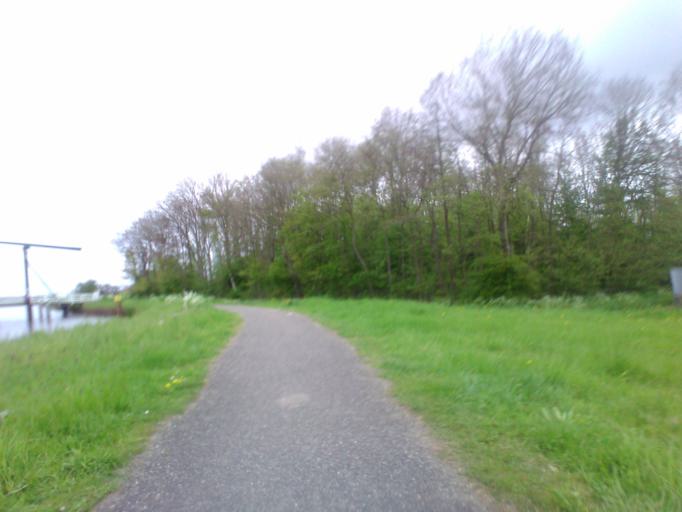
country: NL
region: South Holland
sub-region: Gemeente Gouda
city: Bloemendaal
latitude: 51.9777
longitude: 4.6529
